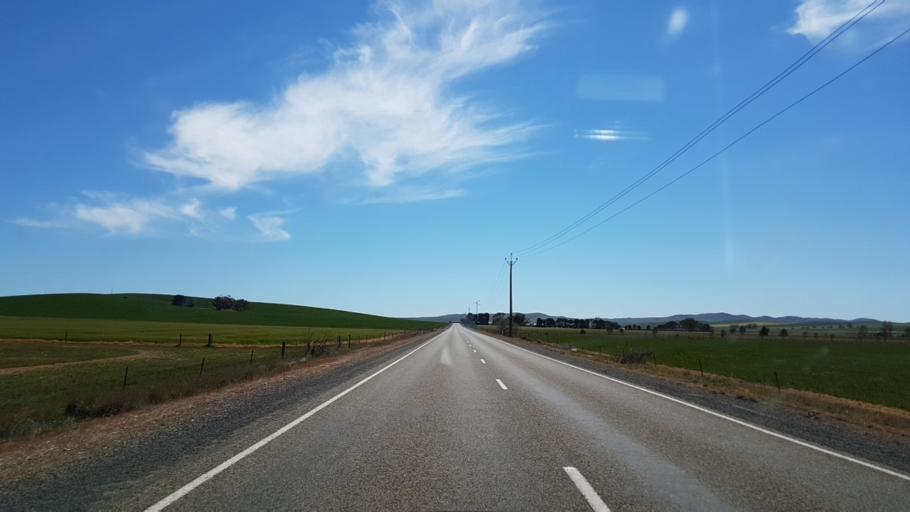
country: AU
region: South Australia
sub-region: Clare and Gilbert Valleys
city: Clare
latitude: -33.8787
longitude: 138.8742
